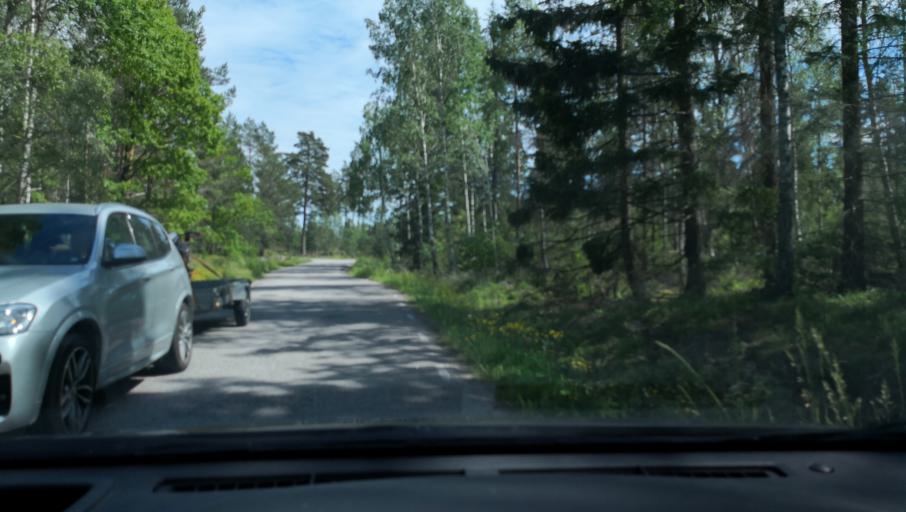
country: SE
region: Uppsala
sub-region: Uppsala Kommun
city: Alsike
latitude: 59.7058
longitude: 17.6744
